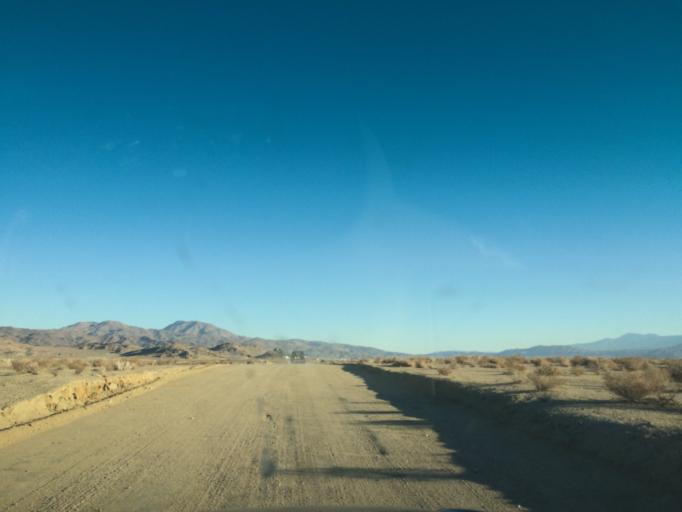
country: US
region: California
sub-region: San Bernardino County
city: Searles Valley
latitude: 35.6651
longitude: -117.3788
